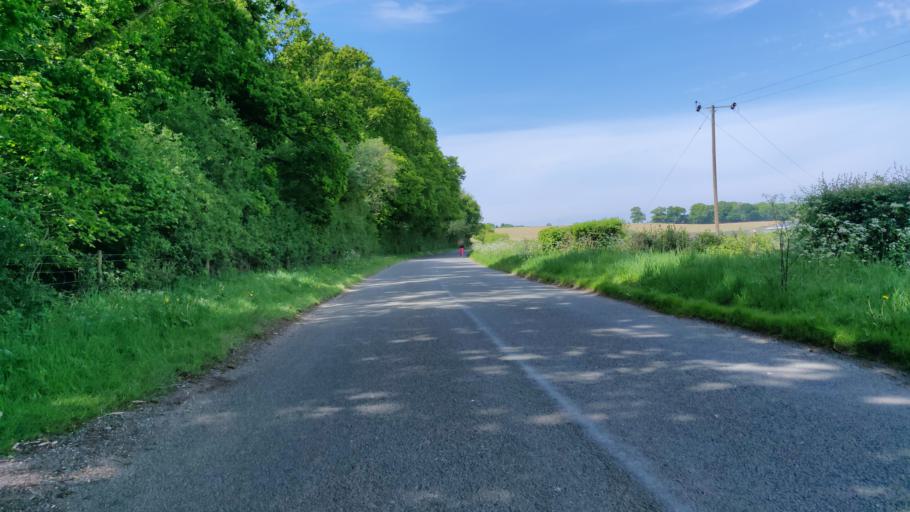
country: GB
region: England
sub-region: West Sussex
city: Southwater
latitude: 51.0472
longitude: -0.3740
